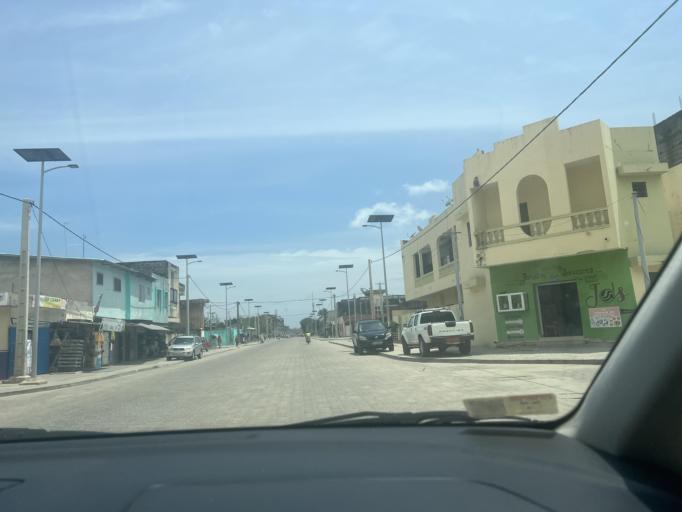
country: BJ
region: Littoral
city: Cotonou
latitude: 6.3873
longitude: 2.4509
